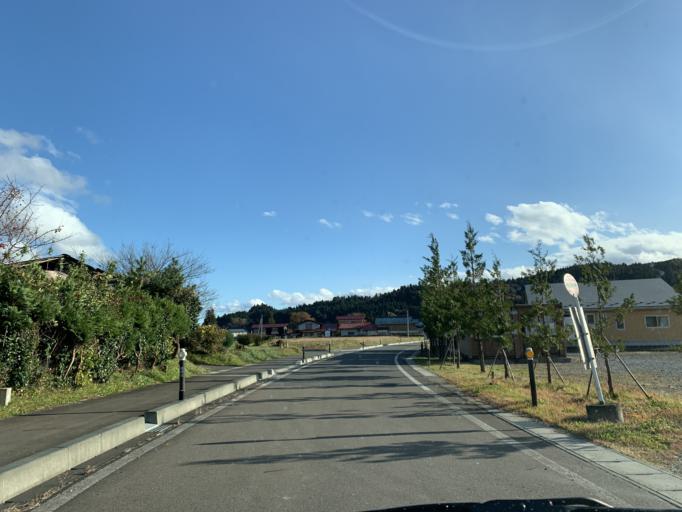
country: JP
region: Iwate
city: Ichinoseki
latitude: 39.0114
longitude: 141.0963
